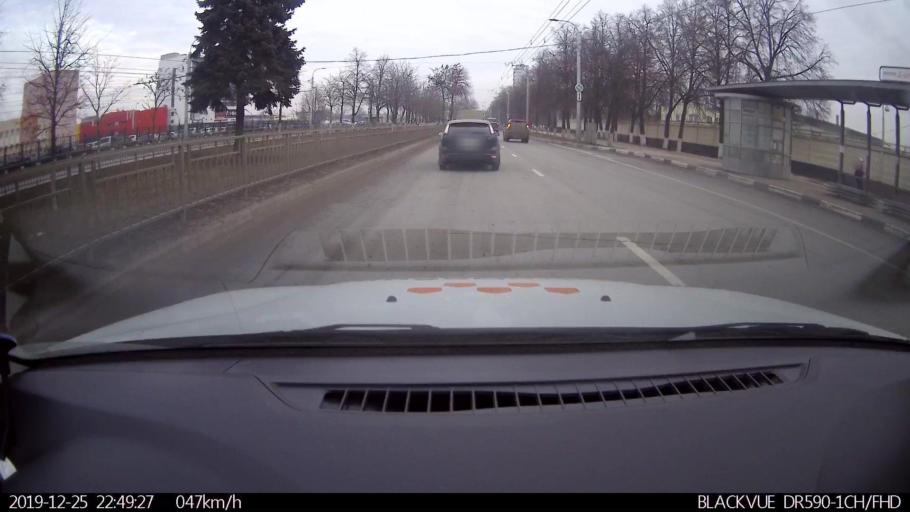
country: RU
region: Nizjnij Novgorod
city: Gorbatovka
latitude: 56.2469
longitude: 43.8765
